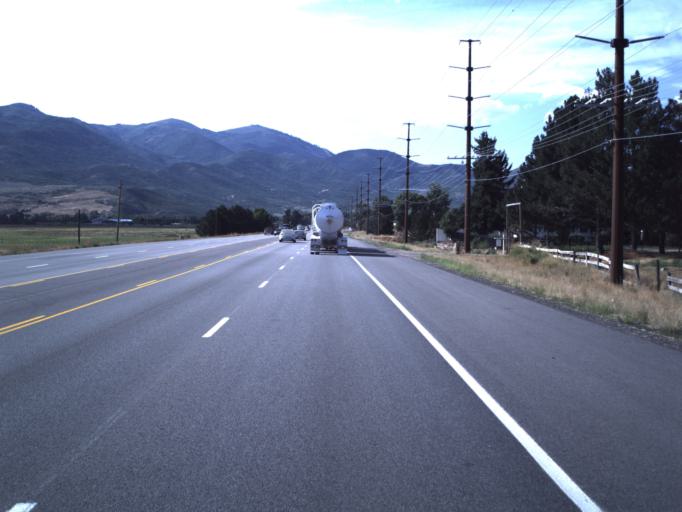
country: US
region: Utah
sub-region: Wasatch County
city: Heber
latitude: 40.5367
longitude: -111.4110
